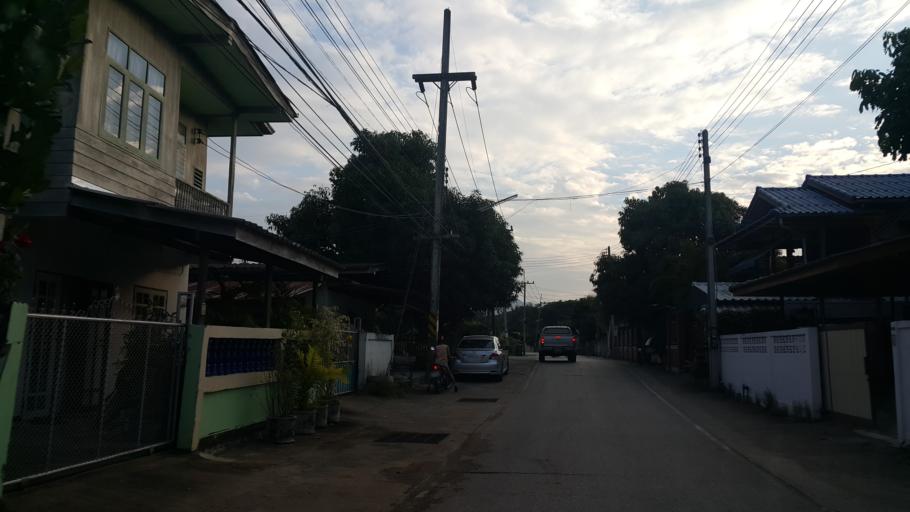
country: TH
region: Lampang
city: Sop Prap
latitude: 17.8744
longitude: 99.3327
